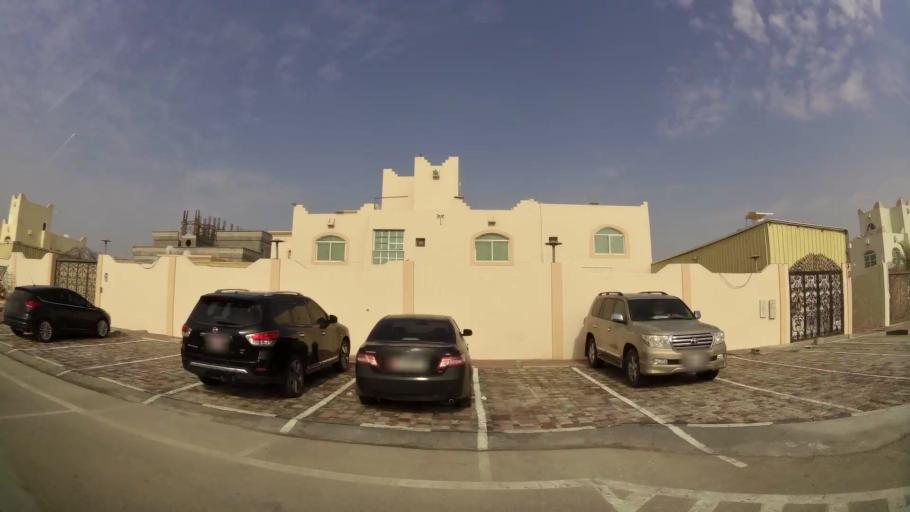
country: AE
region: Abu Dhabi
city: Abu Dhabi
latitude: 24.6583
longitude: 54.7680
